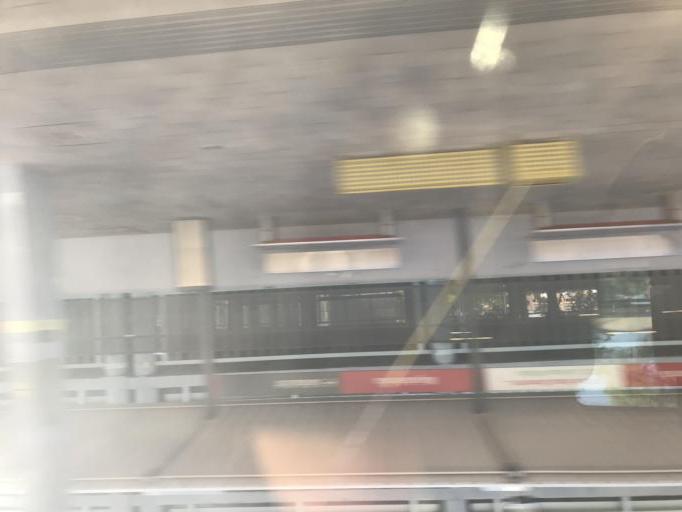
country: ES
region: Madrid
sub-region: Provincia de Madrid
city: Majadahonda
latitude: 40.4740
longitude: -3.8451
